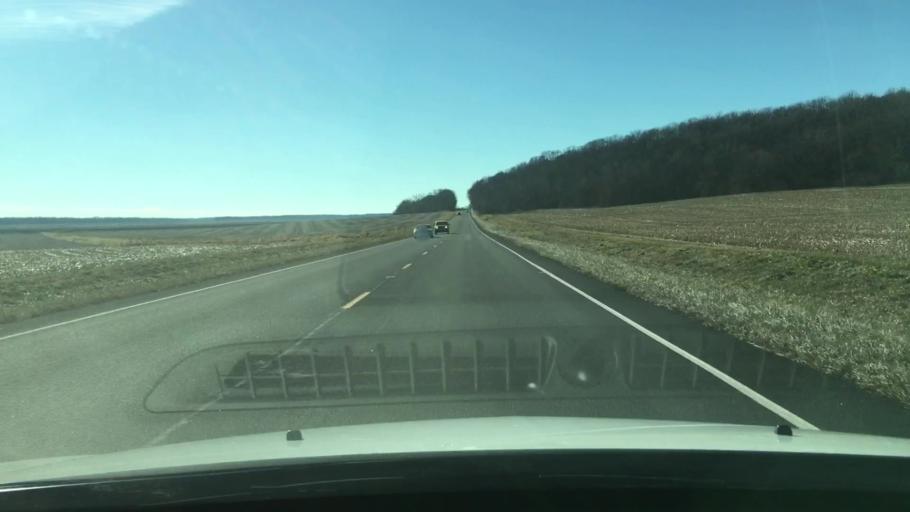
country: US
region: Illinois
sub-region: Fulton County
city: Canton
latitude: 40.4381
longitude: -89.9687
